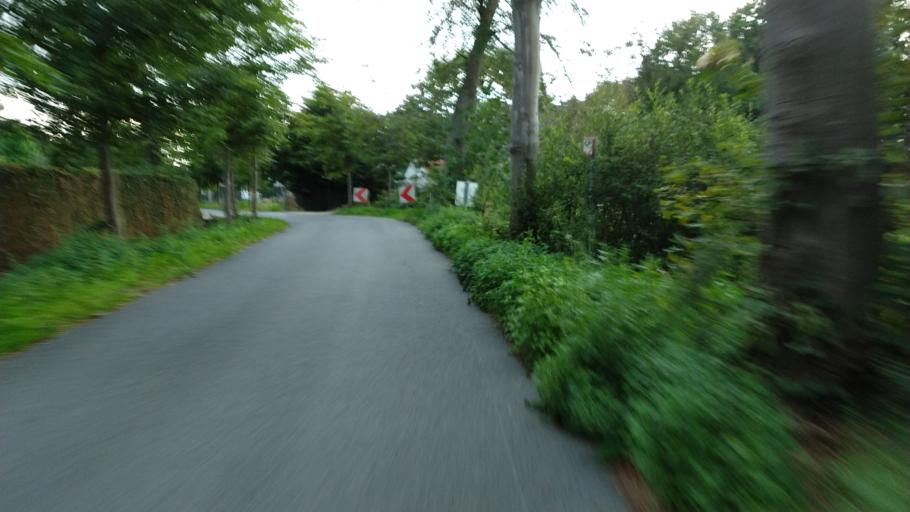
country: BE
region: Flanders
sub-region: Provincie Oost-Vlaanderen
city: Aalter
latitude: 51.0794
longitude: 3.4799
